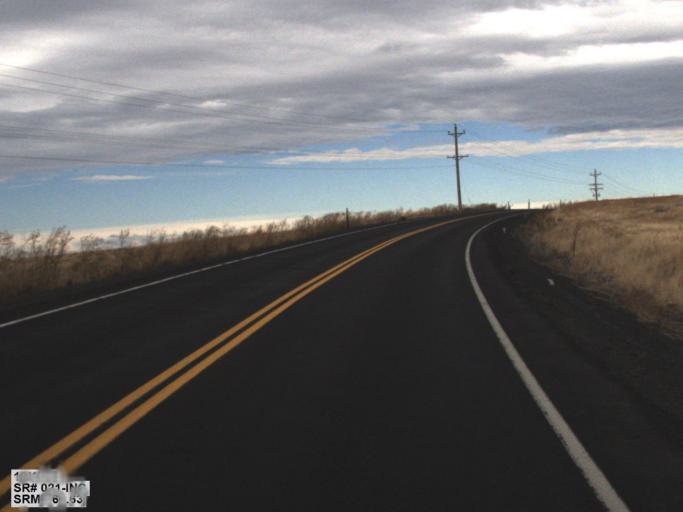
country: US
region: Washington
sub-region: Adams County
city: Ritzville
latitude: 47.4267
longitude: -118.7125
